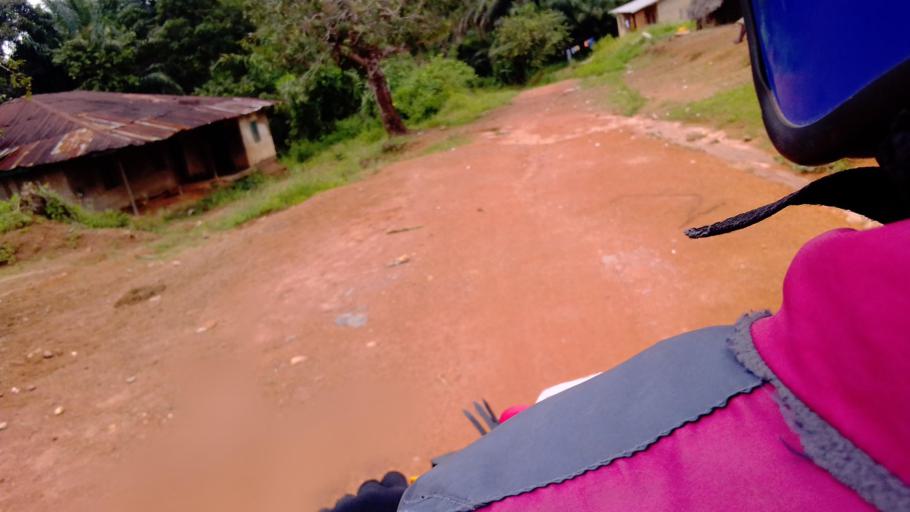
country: SL
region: Eastern Province
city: Koidu
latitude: 8.6580
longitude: -10.9340
